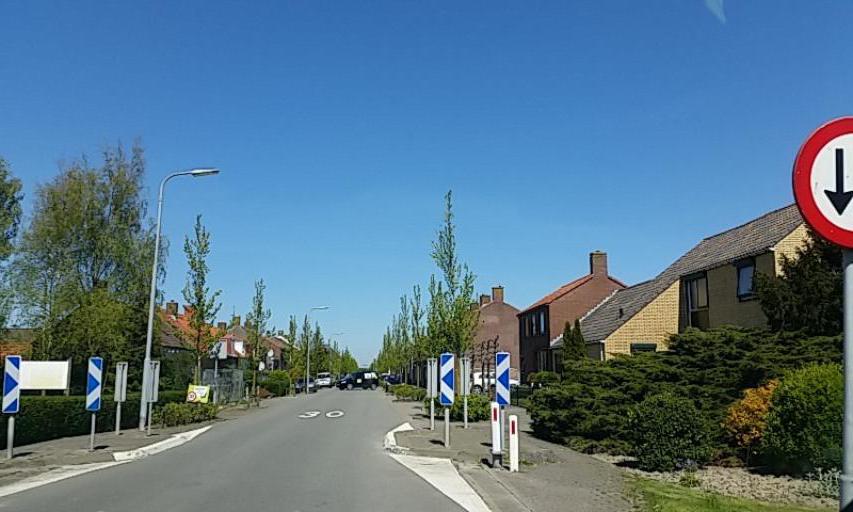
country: NL
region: Zeeland
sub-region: Gemeente Borsele
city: Borssele
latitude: 51.3664
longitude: 3.6604
